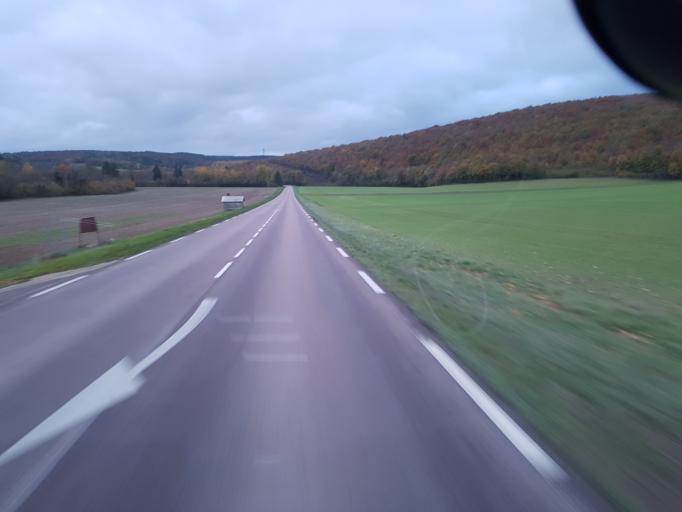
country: FR
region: Champagne-Ardenne
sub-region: Departement de l'Aube
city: Mussy-sur-Seine
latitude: 48.0043
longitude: 4.4743
